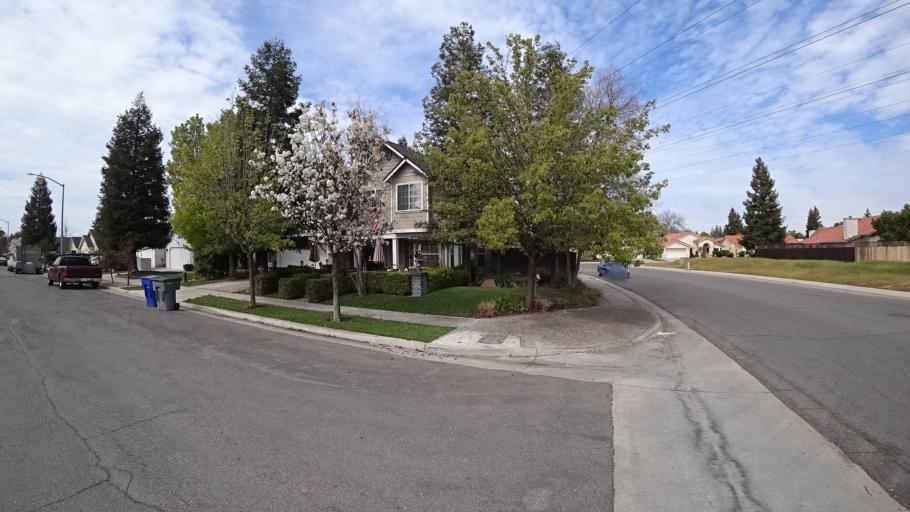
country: US
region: California
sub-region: Fresno County
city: West Park
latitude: 36.8303
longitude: -119.8921
